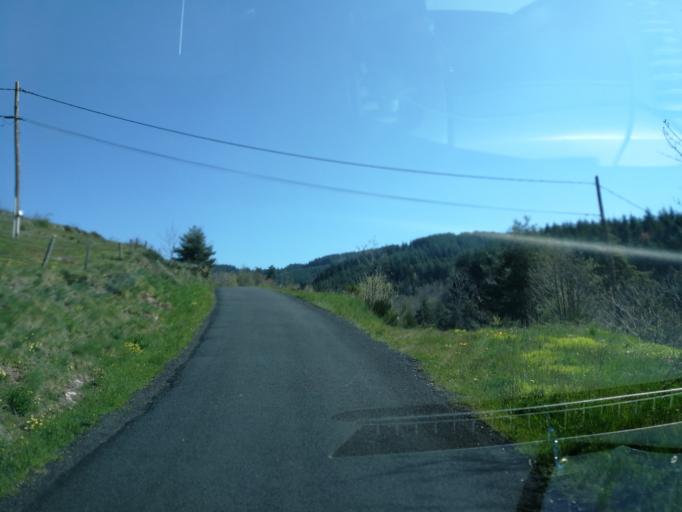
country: FR
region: Rhone-Alpes
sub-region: Departement de l'Ardeche
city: Le Cheylard
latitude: 44.9354
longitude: 4.4235
